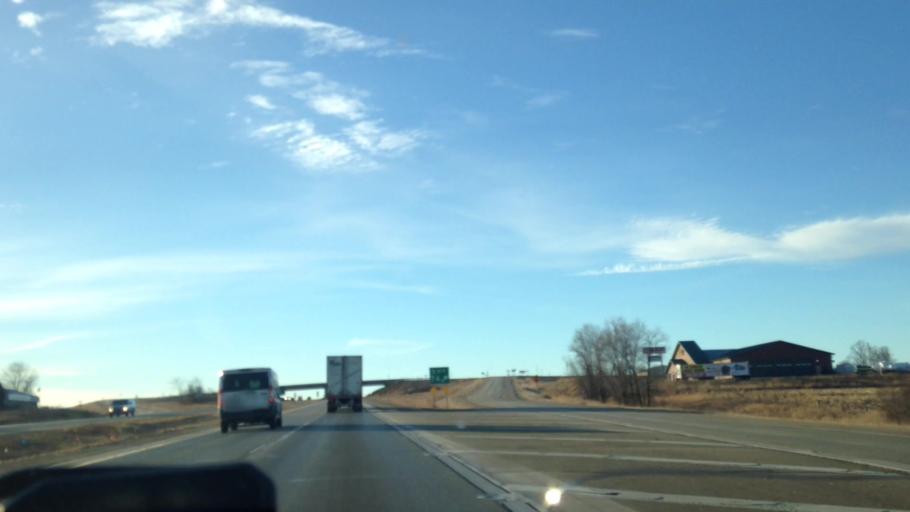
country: US
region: Wisconsin
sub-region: Dodge County
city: Theresa
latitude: 43.4777
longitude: -88.3672
